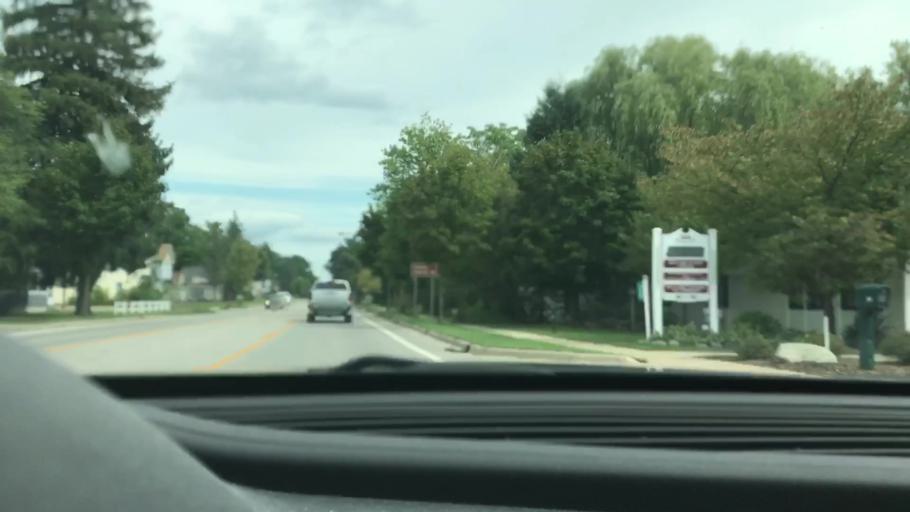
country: US
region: Michigan
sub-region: Antrim County
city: Bellaire
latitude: 44.9754
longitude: -85.2060
